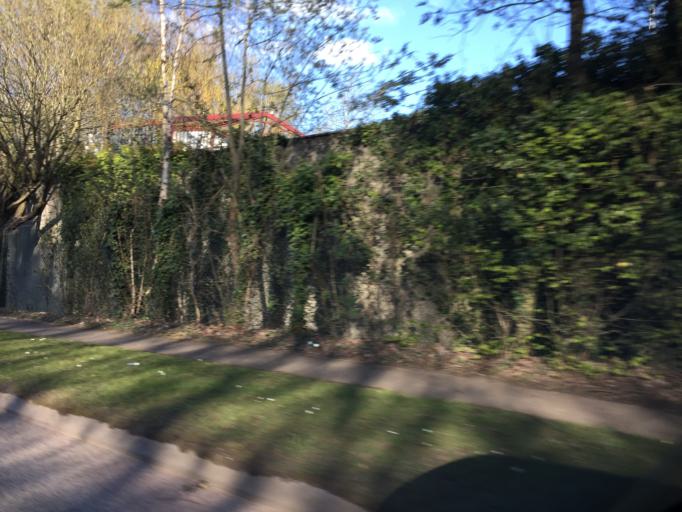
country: GB
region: Wales
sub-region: Torfaen County Borough
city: Cwmbran
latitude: 51.6640
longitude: -3.0226
